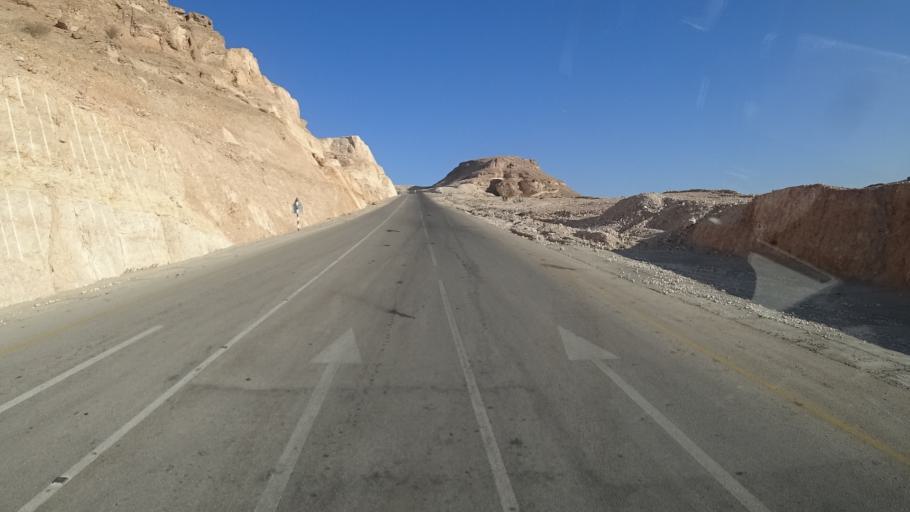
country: YE
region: Al Mahrah
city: Hawf
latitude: 17.0941
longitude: 53.0593
